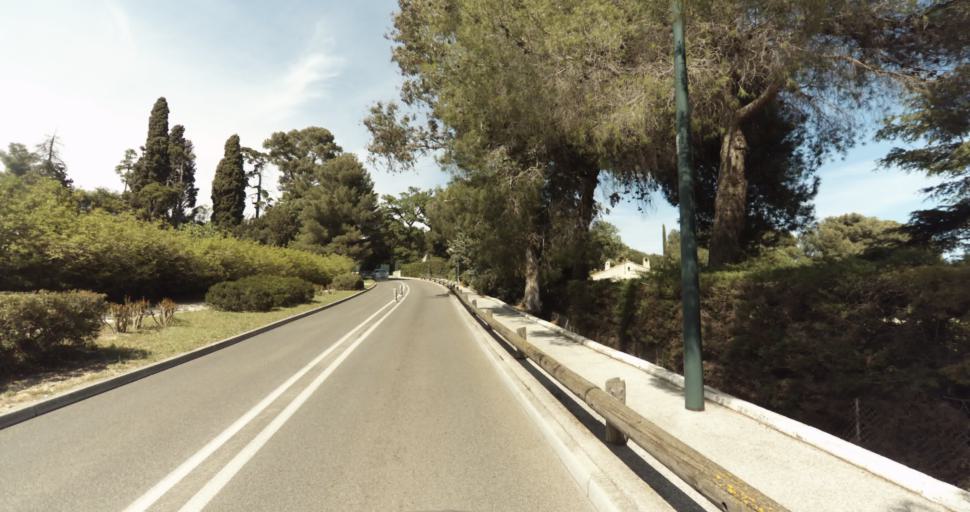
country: FR
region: Provence-Alpes-Cote d'Azur
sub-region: Departement du Var
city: Hyeres
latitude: 43.0932
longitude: 6.1243
